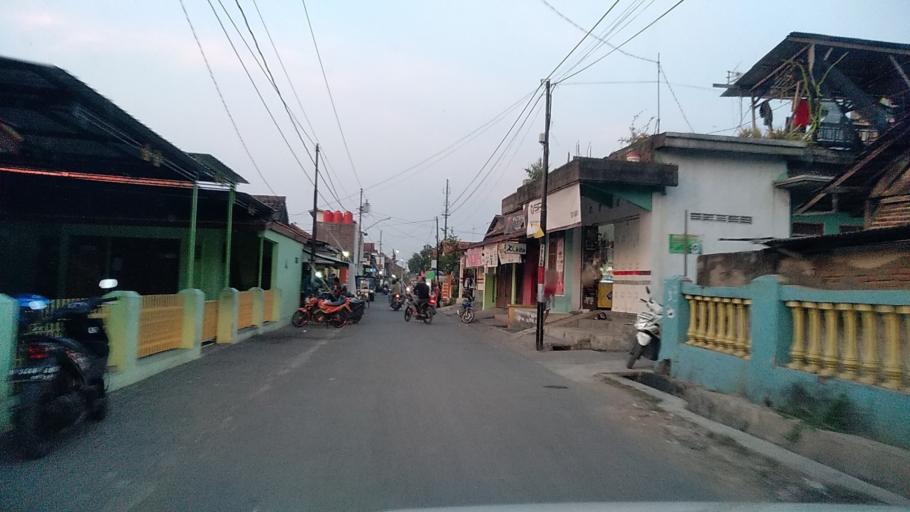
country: ID
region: Central Java
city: Semarang
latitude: -6.9743
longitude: 110.3325
